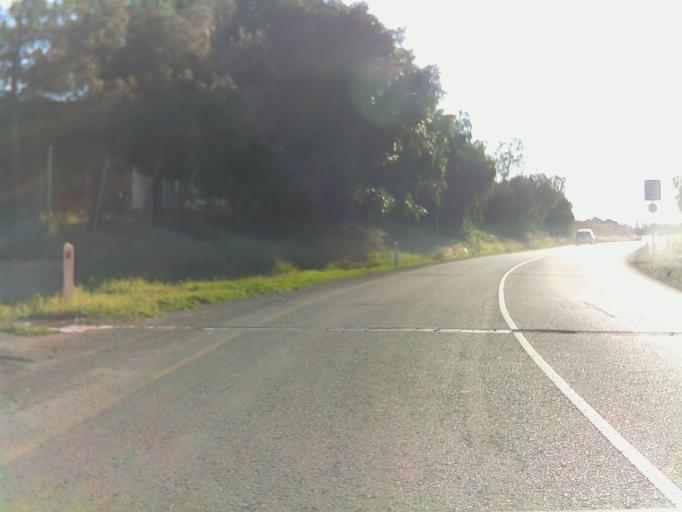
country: CY
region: Pafos
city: Paphos
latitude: 34.7381
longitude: 32.4868
